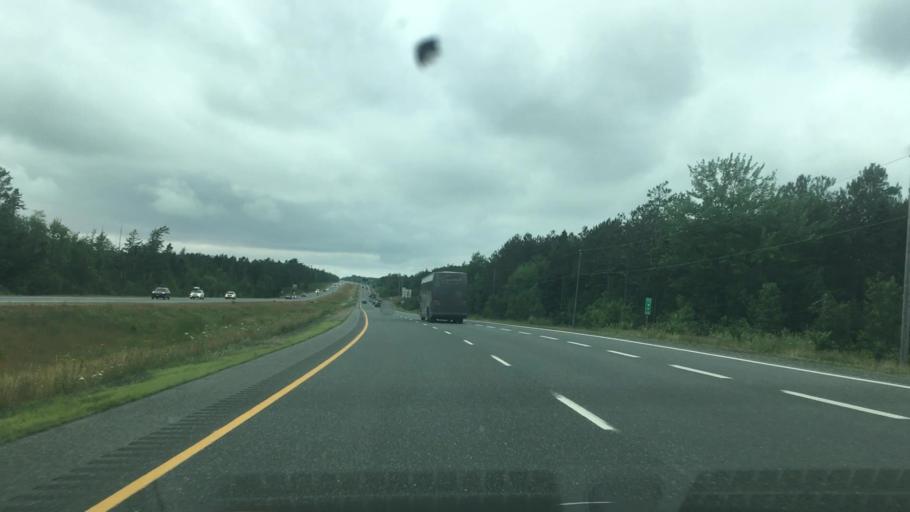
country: CA
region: Nova Scotia
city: Truro
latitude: 45.3990
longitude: -63.4369
